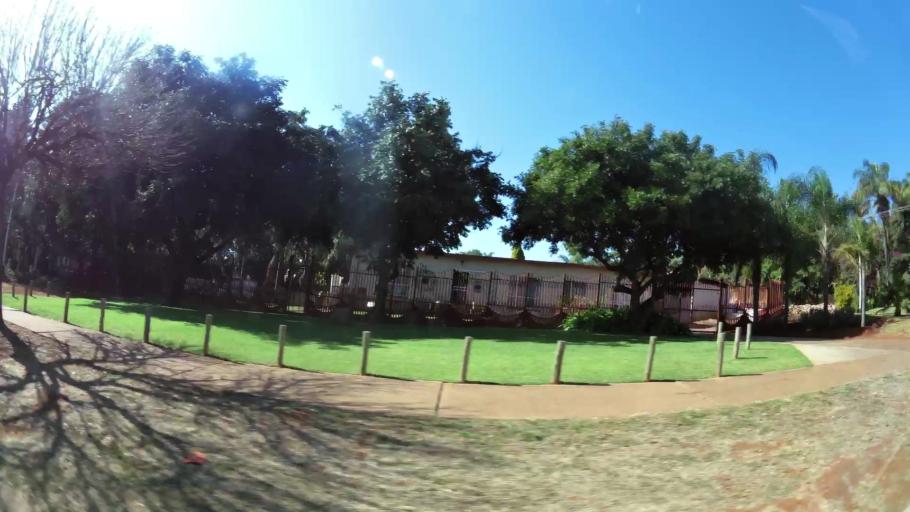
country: ZA
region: Gauteng
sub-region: City of Tshwane Metropolitan Municipality
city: Pretoria
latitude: -25.6822
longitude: 28.2161
